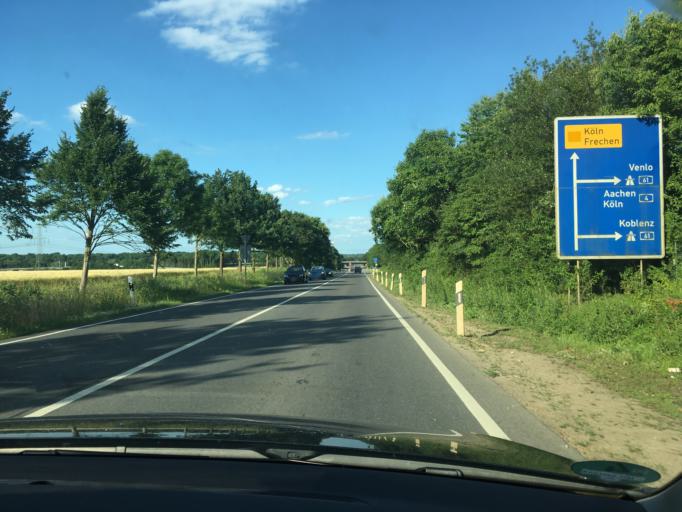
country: DE
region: North Rhine-Westphalia
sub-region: Regierungsbezirk Koln
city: Kerpen
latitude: 50.8553
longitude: 6.7095
